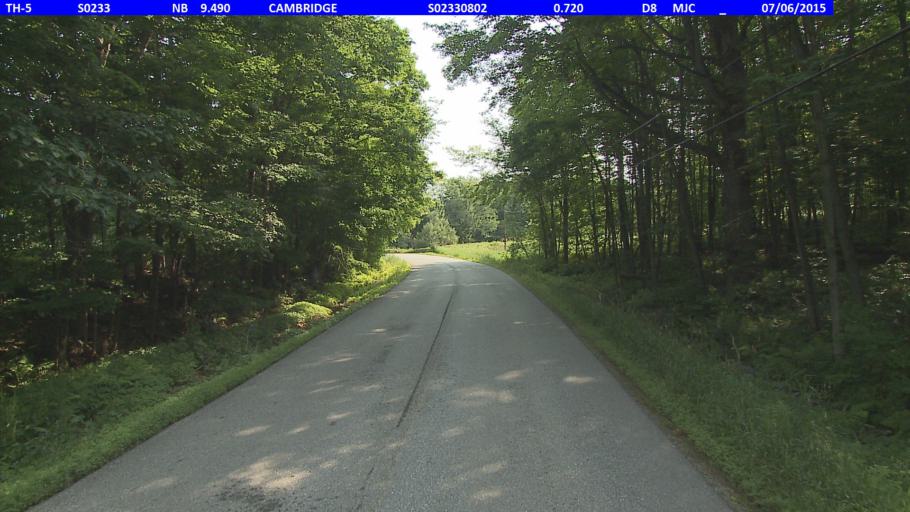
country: US
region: Vermont
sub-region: Chittenden County
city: Jericho
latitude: 44.5931
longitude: -72.8598
